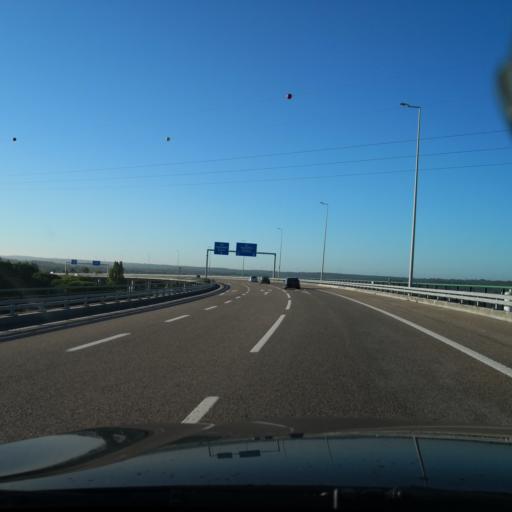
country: PT
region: Evora
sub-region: Vendas Novas
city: Vendas Novas
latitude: 38.6048
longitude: -8.6485
